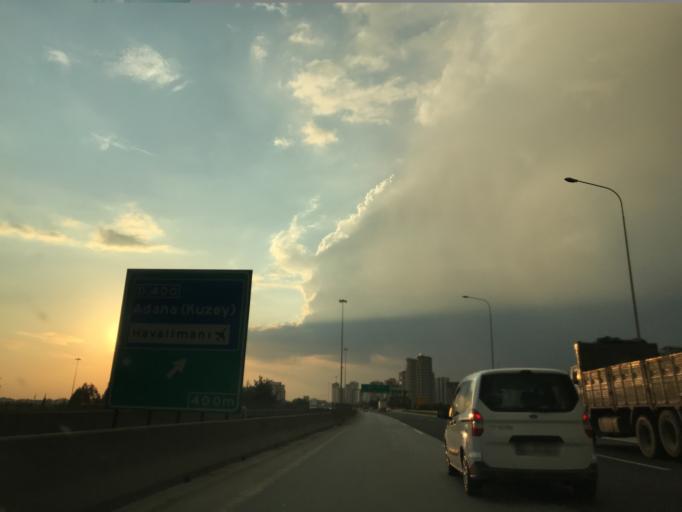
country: TR
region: Adana
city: Seyhan
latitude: 37.0325
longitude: 35.2561
